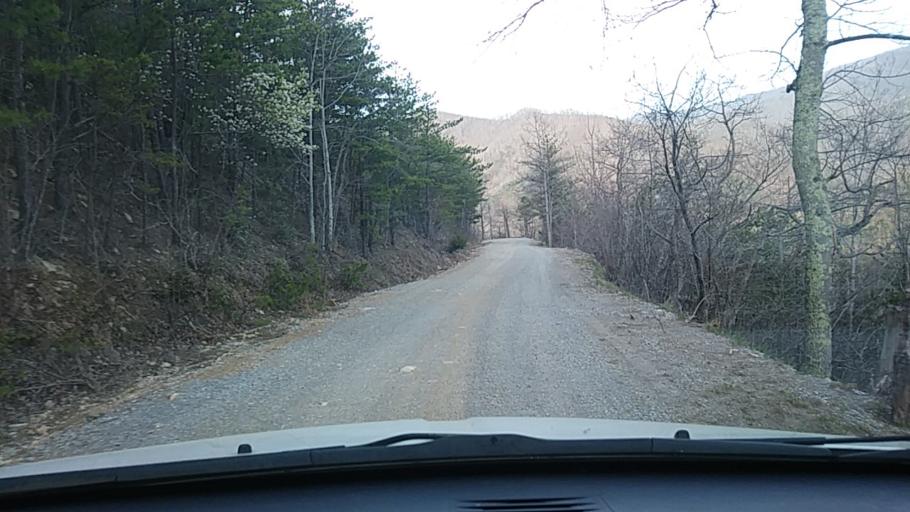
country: US
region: Tennessee
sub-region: Greene County
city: Tusculum
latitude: 36.0838
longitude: -82.6863
